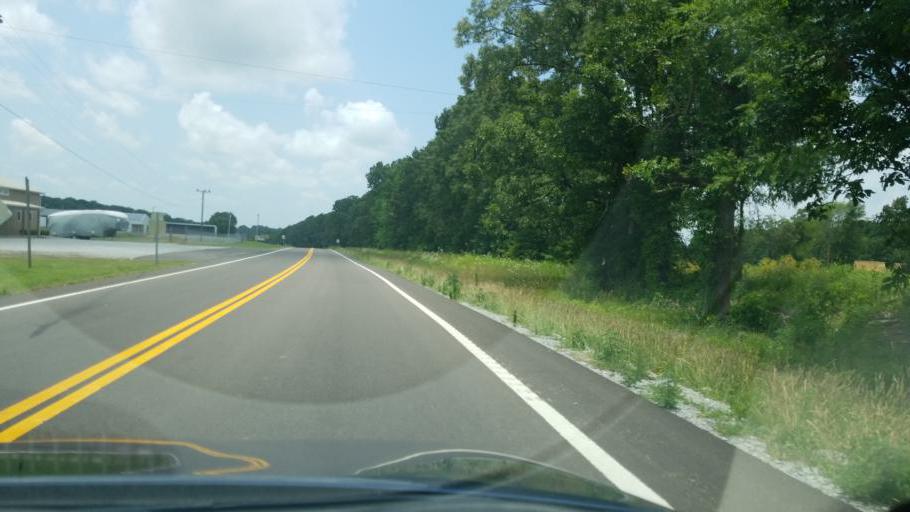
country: US
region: Tennessee
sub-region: Carroll County
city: Huntingdon
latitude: 36.0302
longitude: -88.3557
